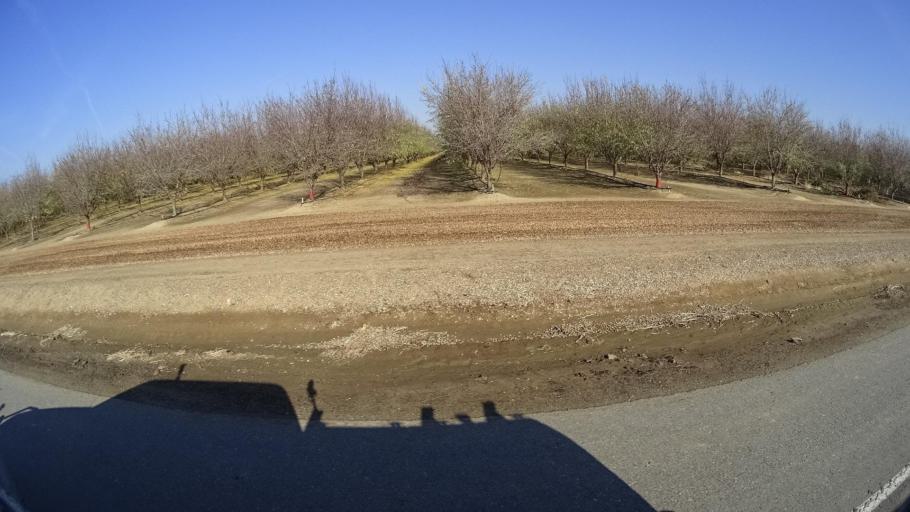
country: US
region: California
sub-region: Kern County
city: Weedpatch
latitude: 35.1942
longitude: -118.8936
